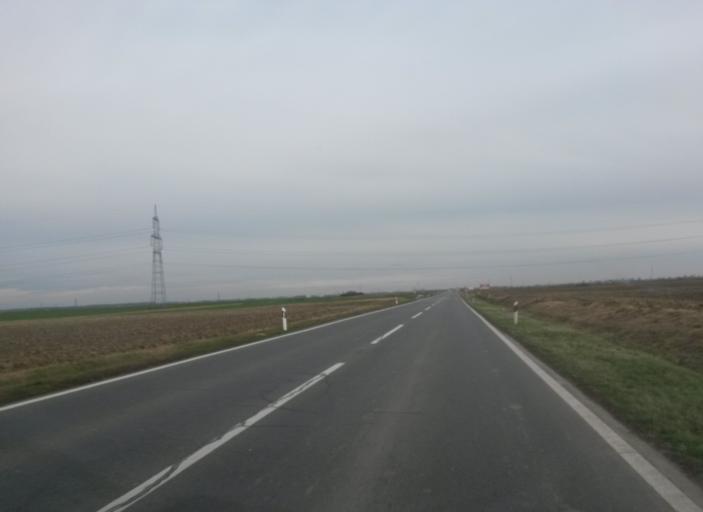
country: HR
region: Osjecko-Baranjska
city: Cepin
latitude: 45.5395
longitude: 18.5807
